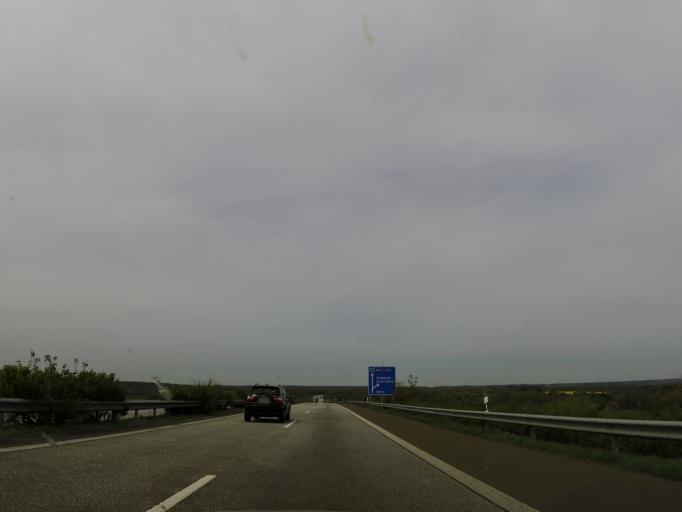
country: DE
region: Schleswig-Holstein
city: Schafstedt
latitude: 54.0713
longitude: 9.3074
